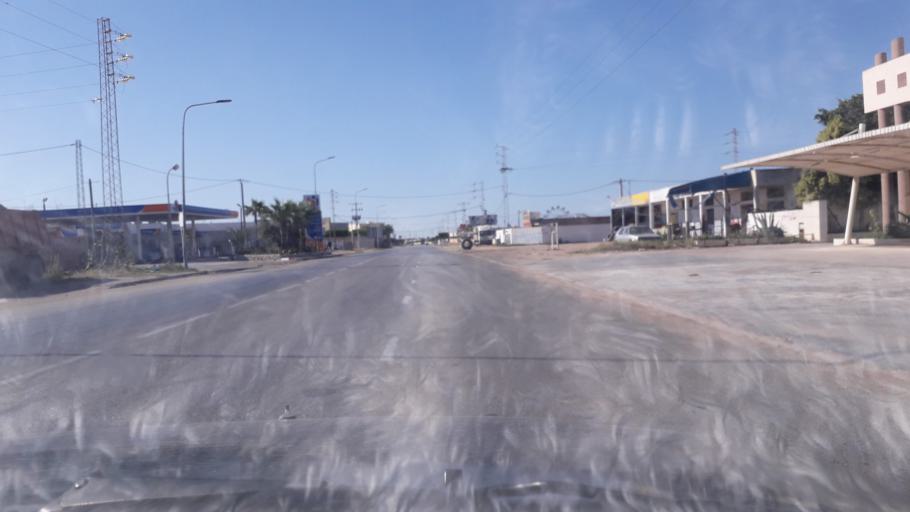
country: TN
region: Safaqis
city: Al Qarmadah
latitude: 34.8486
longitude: 10.7617
